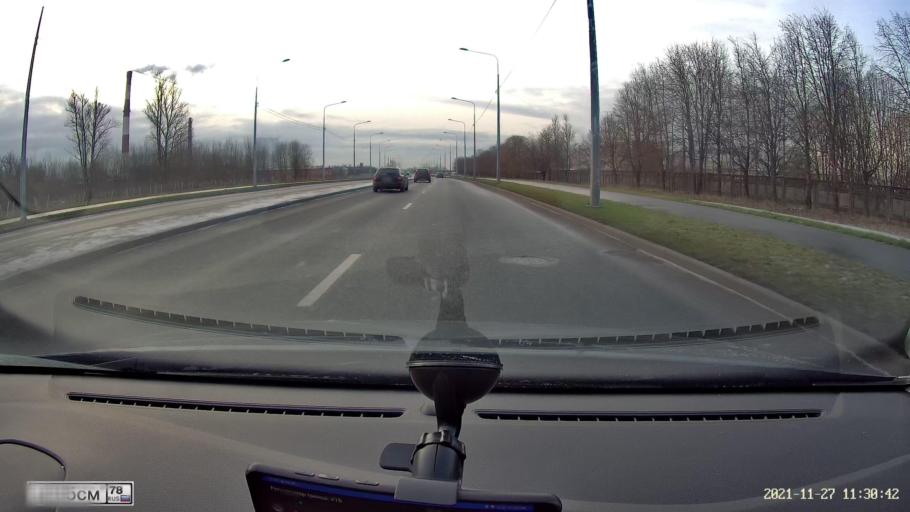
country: RU
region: St.-Petersburg
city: Krasnoye Selo
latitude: 59.7277
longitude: 30.0549
